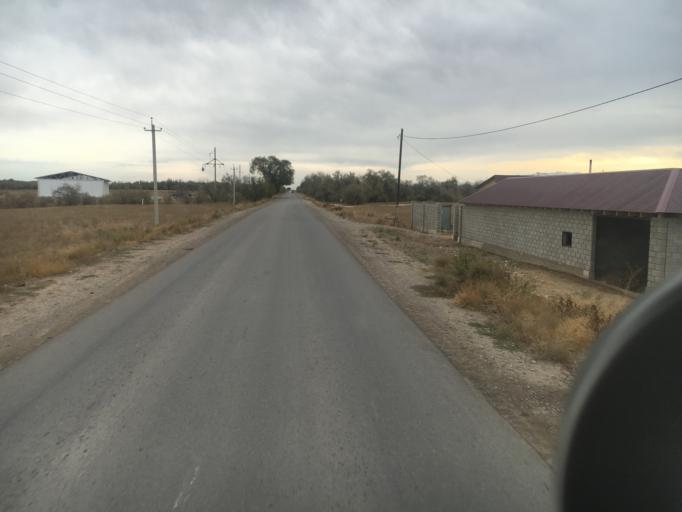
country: KZ
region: Almaty Oblysy
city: Energeticheskiy
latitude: 43.5859
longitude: 77.0692
